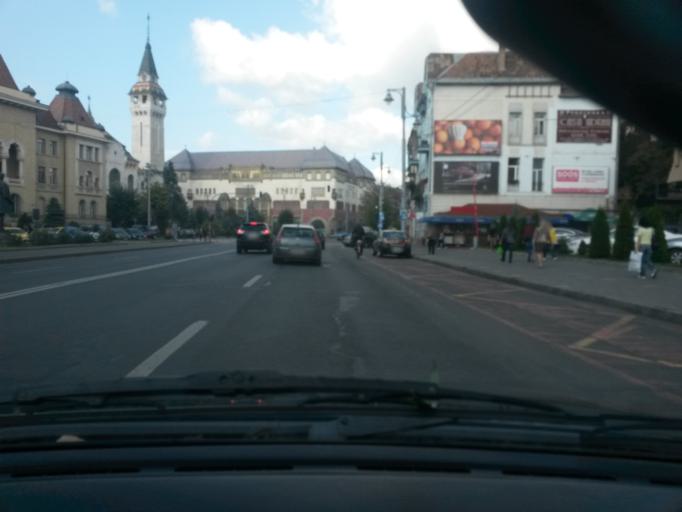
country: RO
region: Mures
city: Targu-Mures
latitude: 46.5417
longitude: 24.5578
